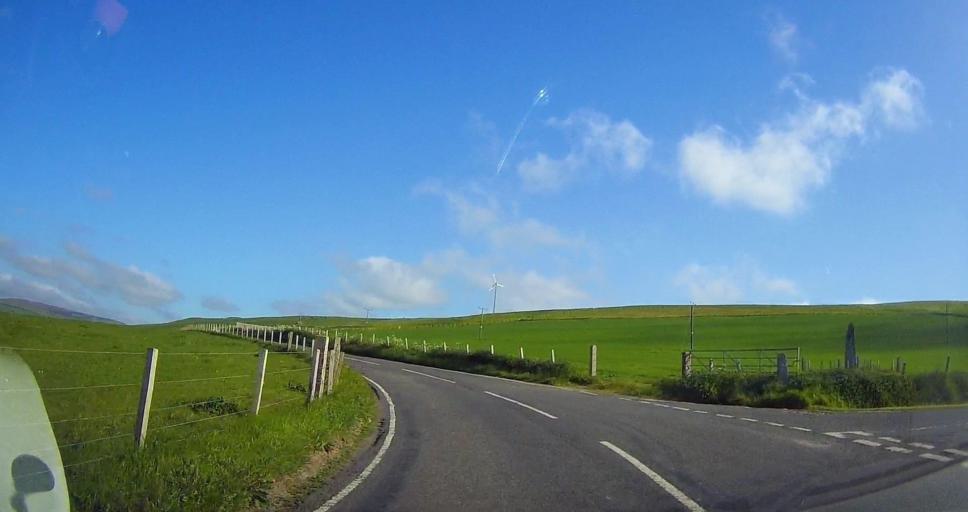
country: GB
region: Scotland
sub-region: Orkney Islands
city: Stromness
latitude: 59.1177
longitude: -3.3059
